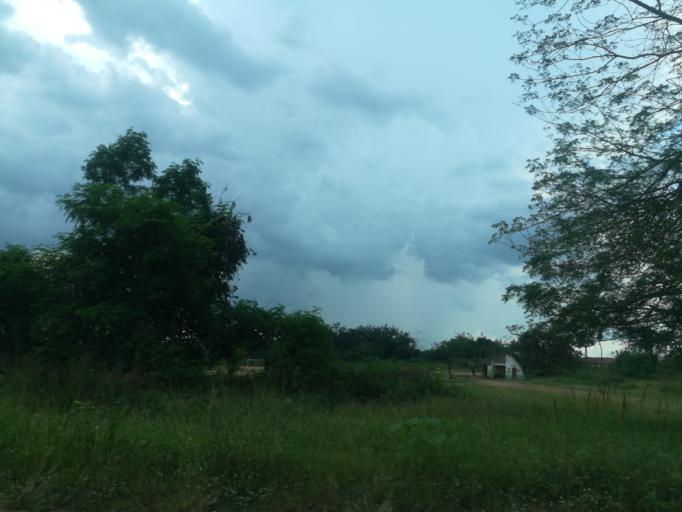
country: NG
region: Oyo
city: Ibadan
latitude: 7.4317
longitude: 3.8928
